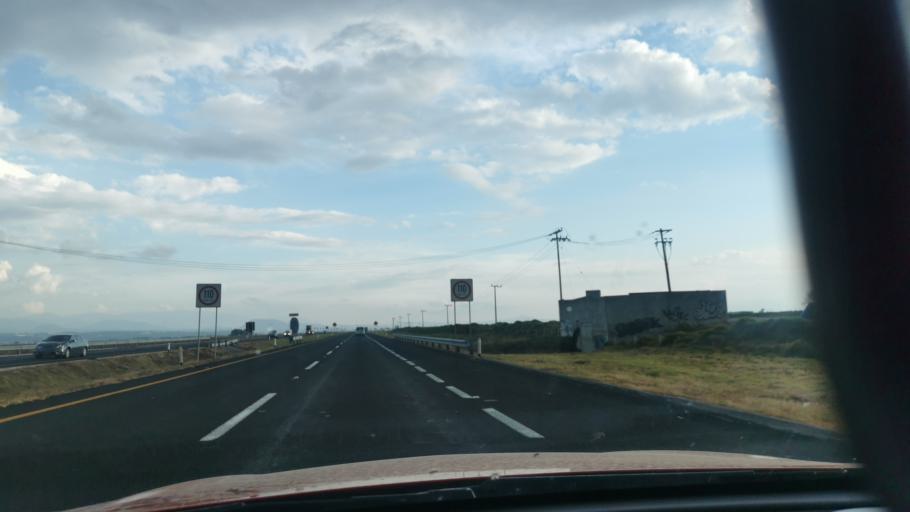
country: MX
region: Mexico
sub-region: Toluca
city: La Constitucion Toltepec
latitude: 19.3545
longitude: -99.5339
